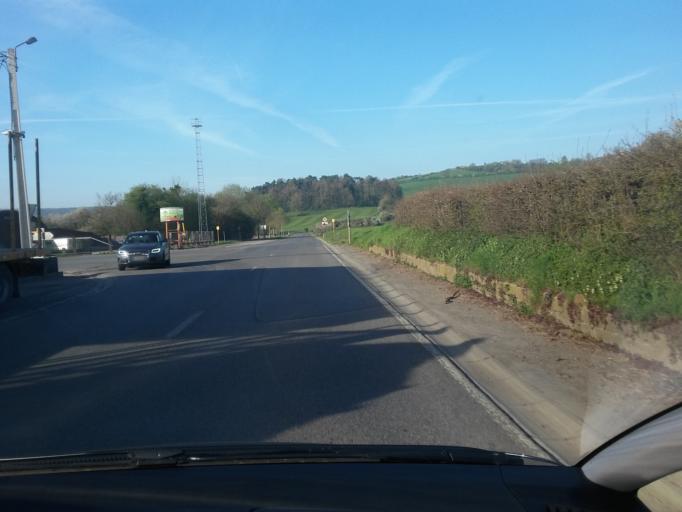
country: BE
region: Wallonia
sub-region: Province du Luxembourg
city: Rouvroy
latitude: 49.5488
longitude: 5.4938
